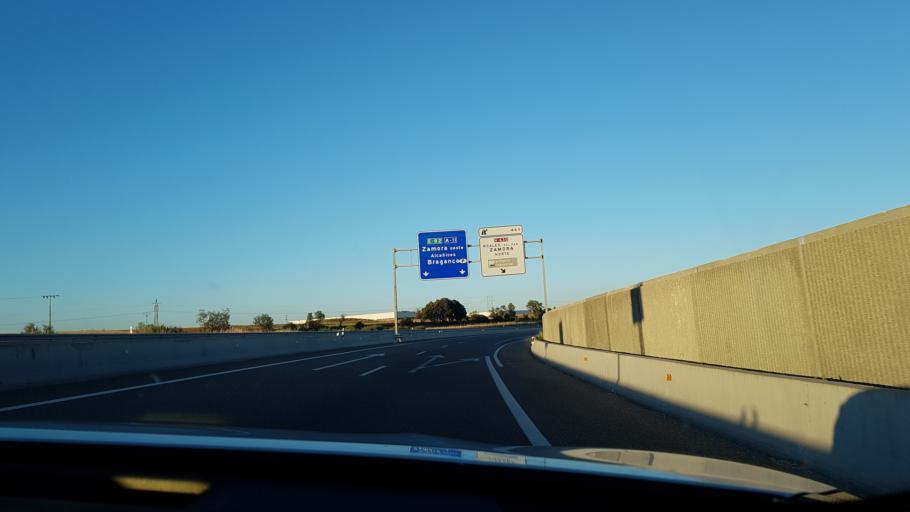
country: ES
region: Castille and Leon
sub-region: Provincia de Zamora
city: Valcabado
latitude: 41.5448
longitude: -5.7584
